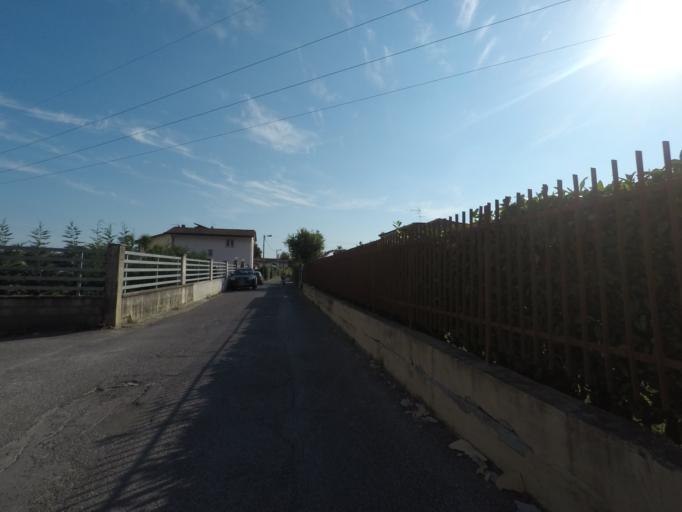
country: IT
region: Tuscany
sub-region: Provincia di Massa-Carrara
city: Massa
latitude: 44.0153
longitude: 10.1408
